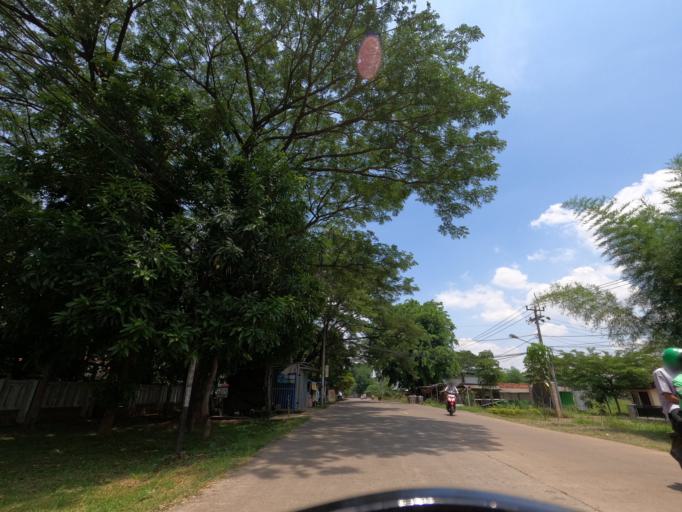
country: ID
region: West Java
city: Pamanukan
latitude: -6.5470
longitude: 107.7661
